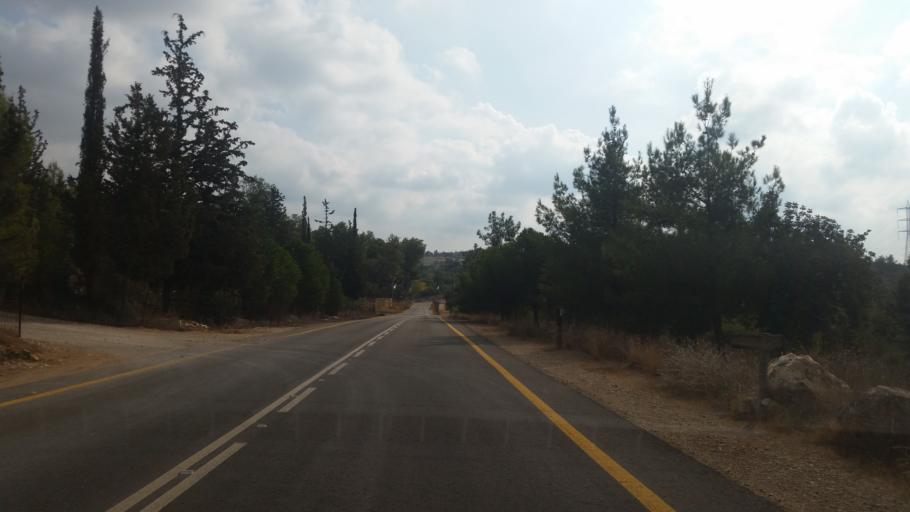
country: IL
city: Hashmonaim
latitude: 31.9206
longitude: 35.0103
